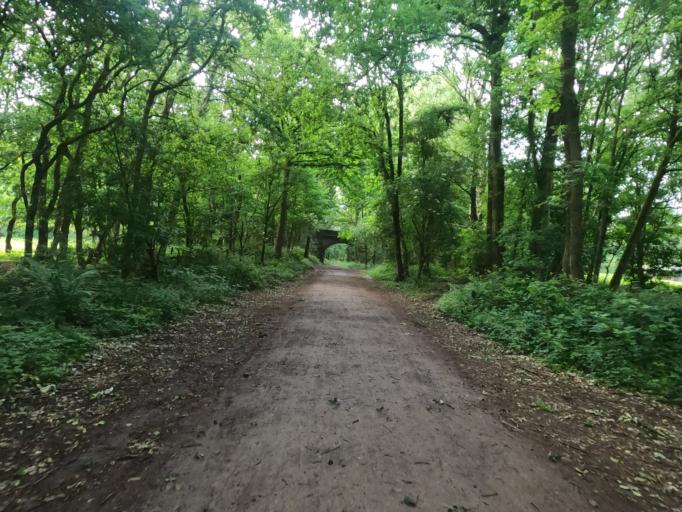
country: GB
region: England
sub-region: Cheshire West and Chester
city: Cuddington
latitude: 53.2178
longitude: -2.6084
